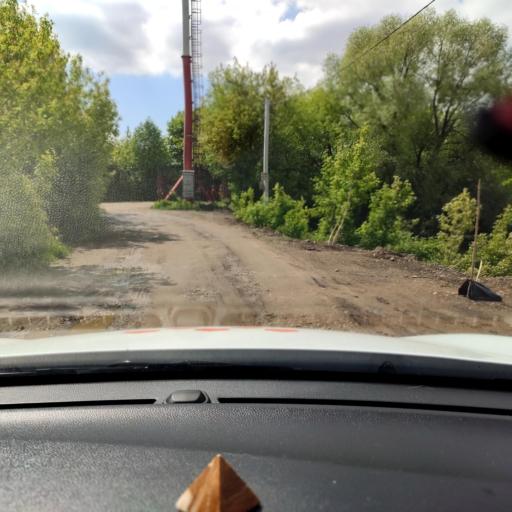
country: RU
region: Tatarstan
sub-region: Gorod Kazan'
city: Kazan
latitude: 55.8586
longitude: 49.1904
